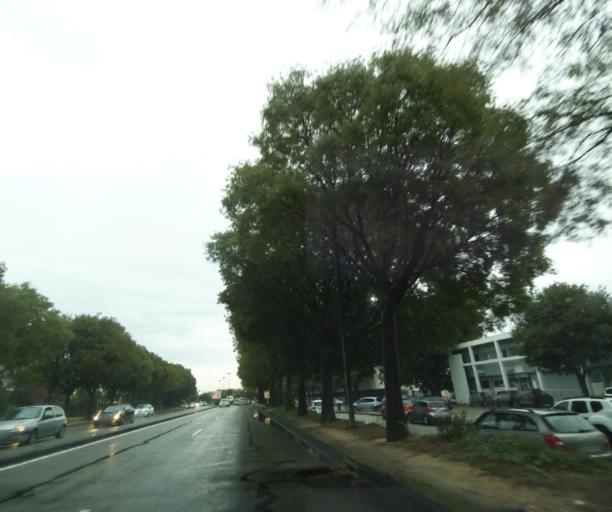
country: FR
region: Languedoc-Roussillon
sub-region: Departement du Gard
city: Nimes
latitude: 43.8318
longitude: 4.3828
